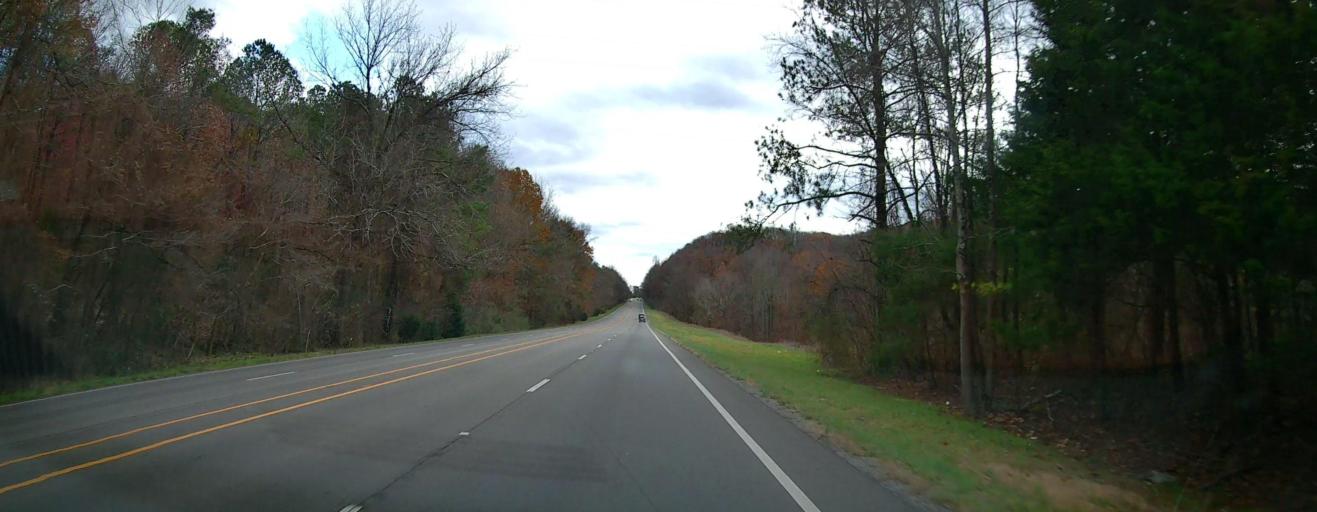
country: US
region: Alabama
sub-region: Morgan County
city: Falkville
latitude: 34.3188
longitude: -87.0002
